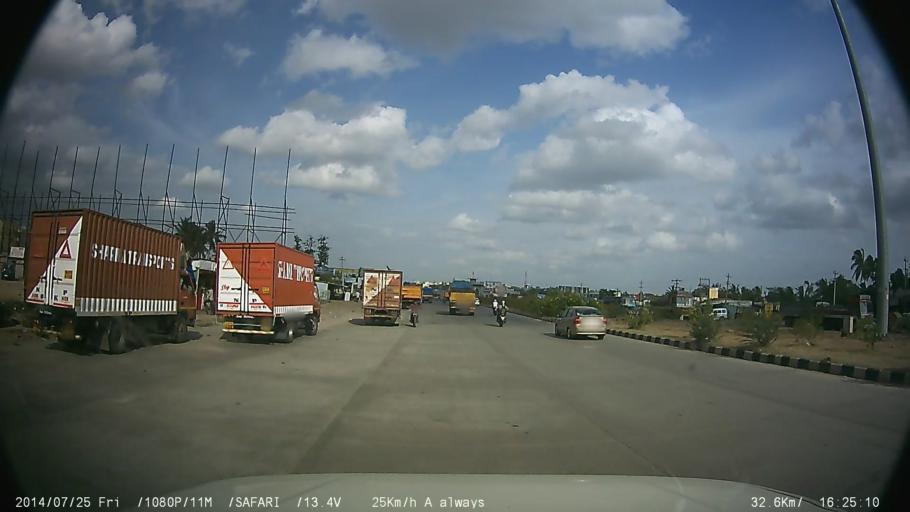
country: IN
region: Tamil Nadu
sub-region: Krishnagiri
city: Hosur
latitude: 12.7760
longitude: 77.7787
